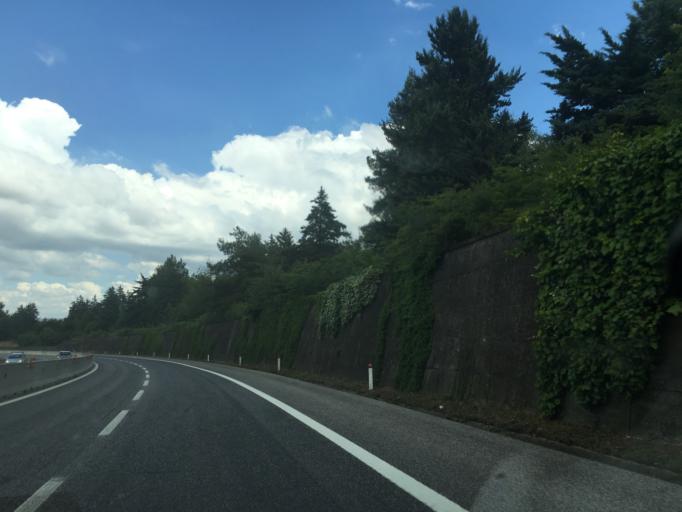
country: IT
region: Campania
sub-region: Provincia di Avellino
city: Grottaminarda
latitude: 41.0601
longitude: 15.0461
